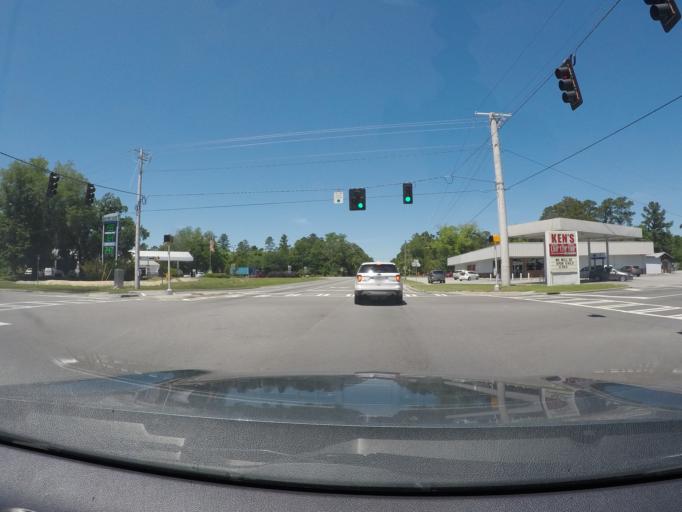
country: US
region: Georgia
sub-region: Effingham County
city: Guyton
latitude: 32.1971
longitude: -81.4380
